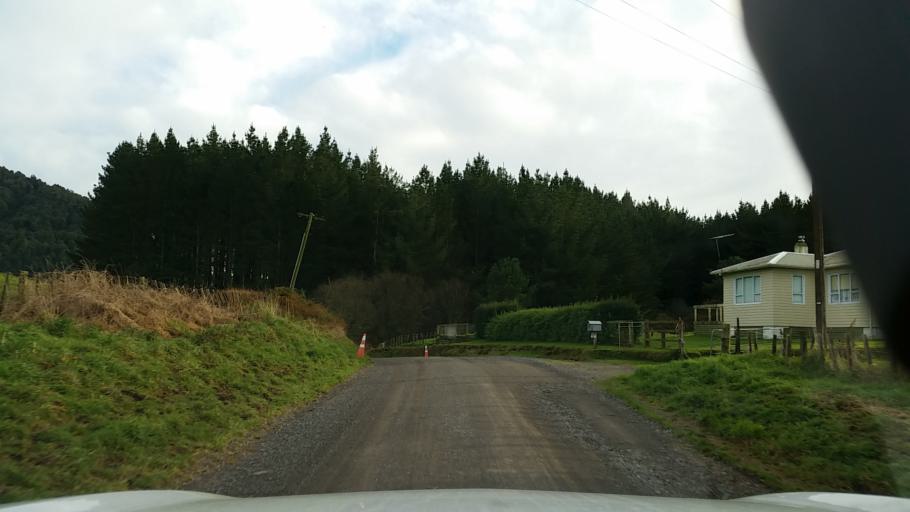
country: NZ
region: Bay of Plenty
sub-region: Rotorua District
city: Rotorua
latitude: -38.2367
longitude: 176.1691
